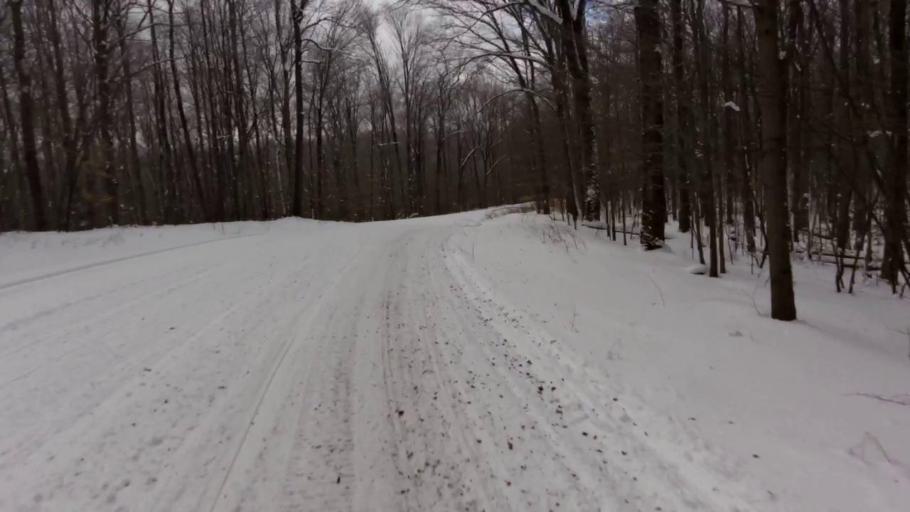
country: US
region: New York
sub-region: Cattaraugus County
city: Salamanca
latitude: 42.0552
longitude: -78.7604
